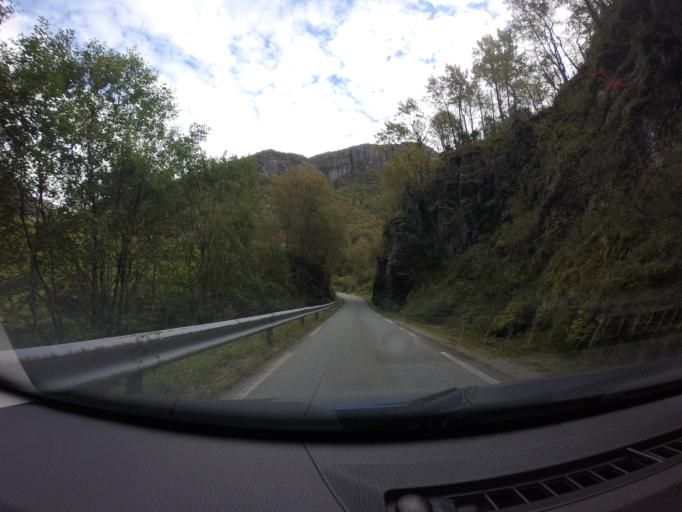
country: NO
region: Rogaland
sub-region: Forsand
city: Forsand
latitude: 58.8517
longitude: 6.3699
